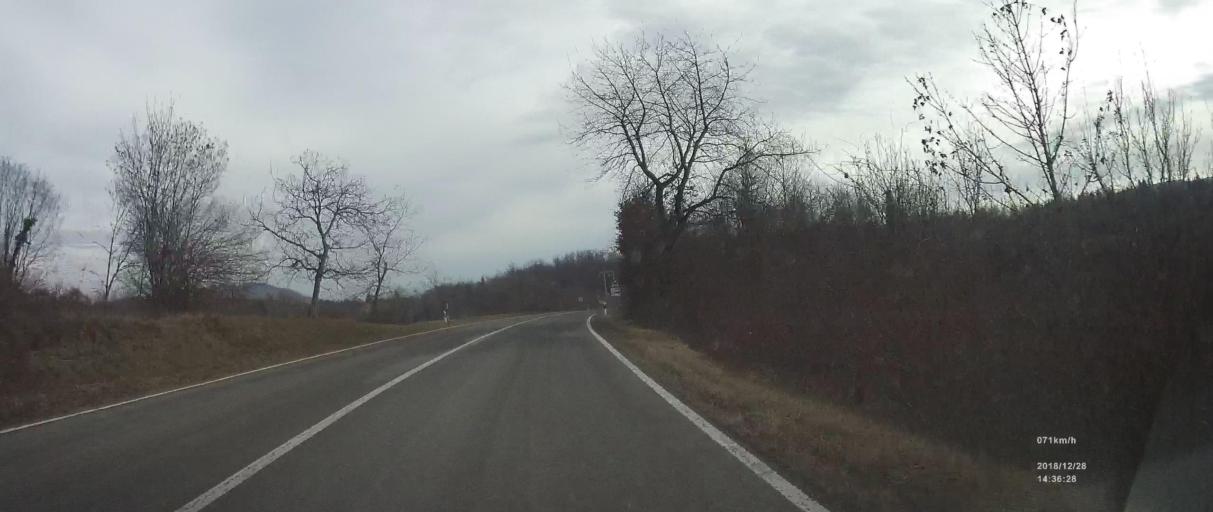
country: HR
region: Primorsko-Goranska
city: Vrbovsko
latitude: 45.4228
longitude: 15.1971
